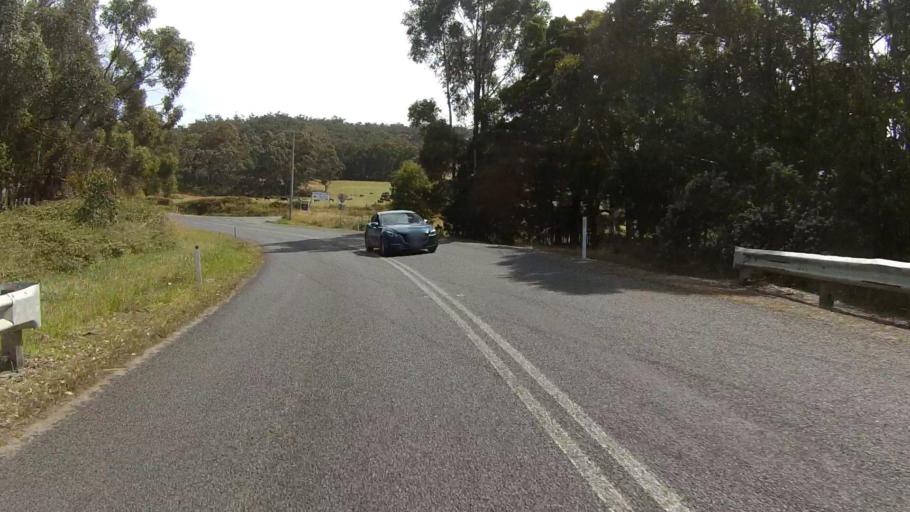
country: AU
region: Tasmania
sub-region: Huon Valley
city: Cygnet
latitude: -43.1852
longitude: 147.1075
